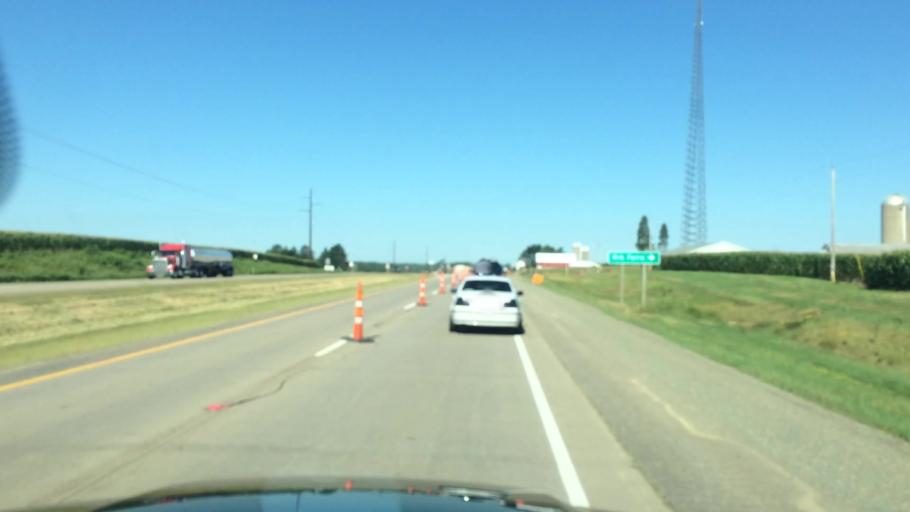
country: US
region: Wisconsin
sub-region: Marathon County
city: Marathon
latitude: 44.9446
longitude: -89.9018
